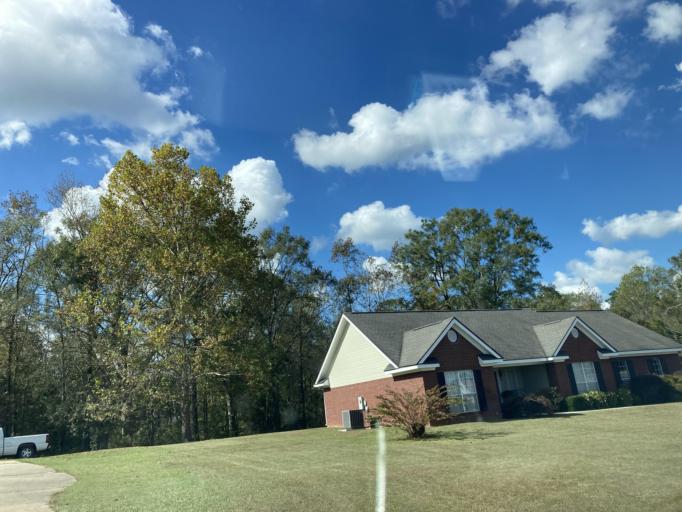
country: US
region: Mississippi
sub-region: Lamar County
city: West Hattiesburg
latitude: 31.2711
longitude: -89.3848
